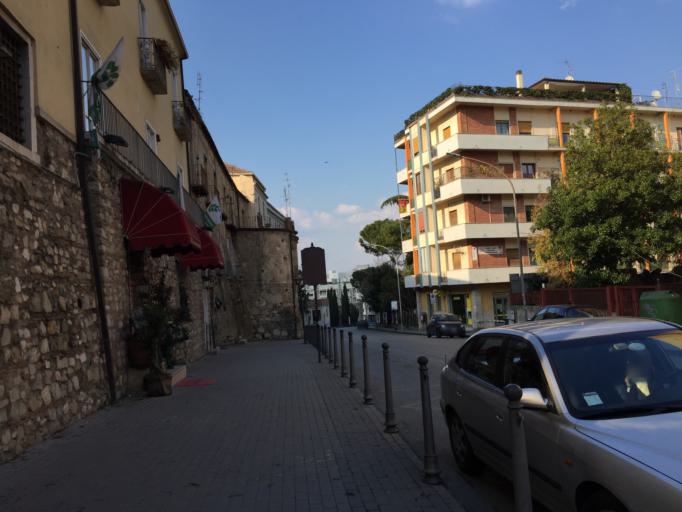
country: IT
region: Campania
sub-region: Provincia di Benevento
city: Benevento
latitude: 41.1302
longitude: 14.7826
